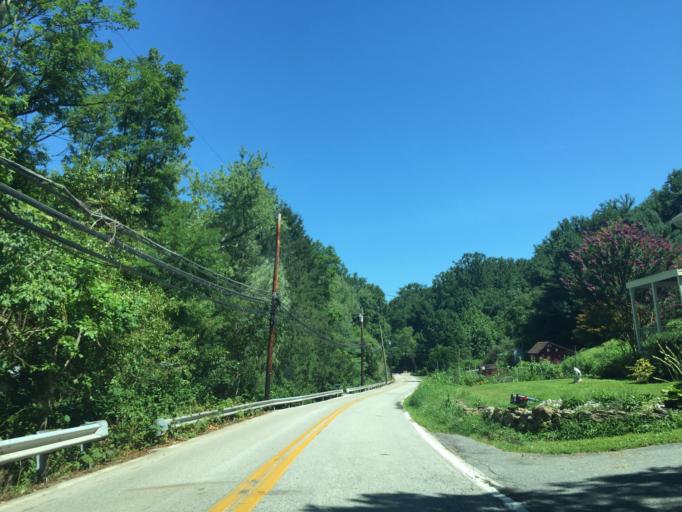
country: US
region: Maryland
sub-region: Baltimore County
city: Cockeysville
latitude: 39.4795
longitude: -76.6162
